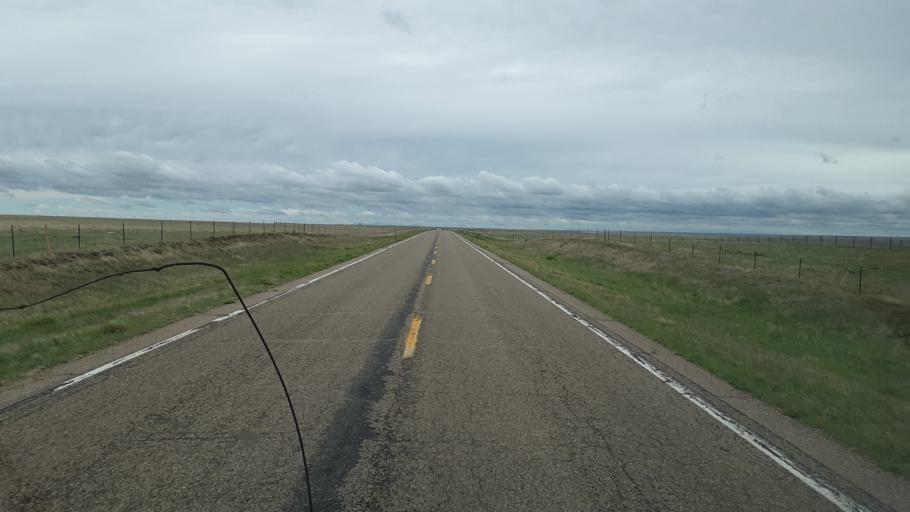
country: US
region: Colorado
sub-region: Lincoln County
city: Hugo
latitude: 38.8522
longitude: -103.7694
